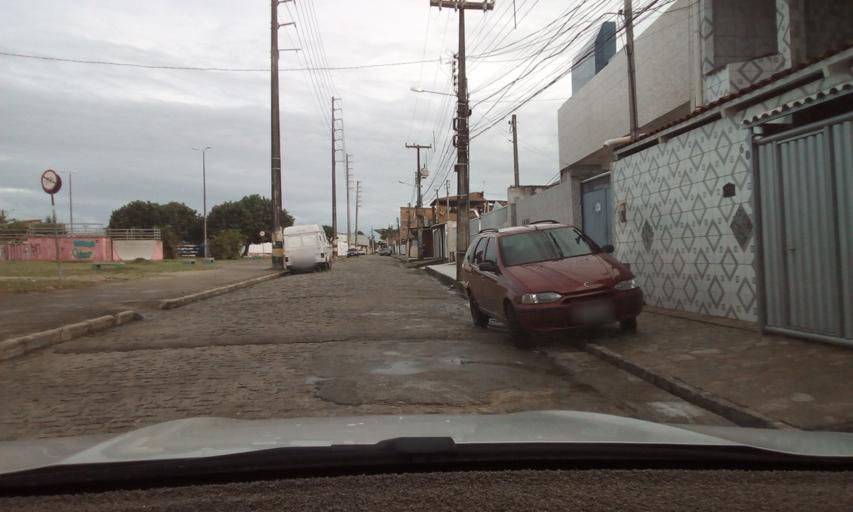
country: BR
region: Paraiba
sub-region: Joao Pessoa
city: Joao Pessoa
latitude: -7.1478
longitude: -34.8750
